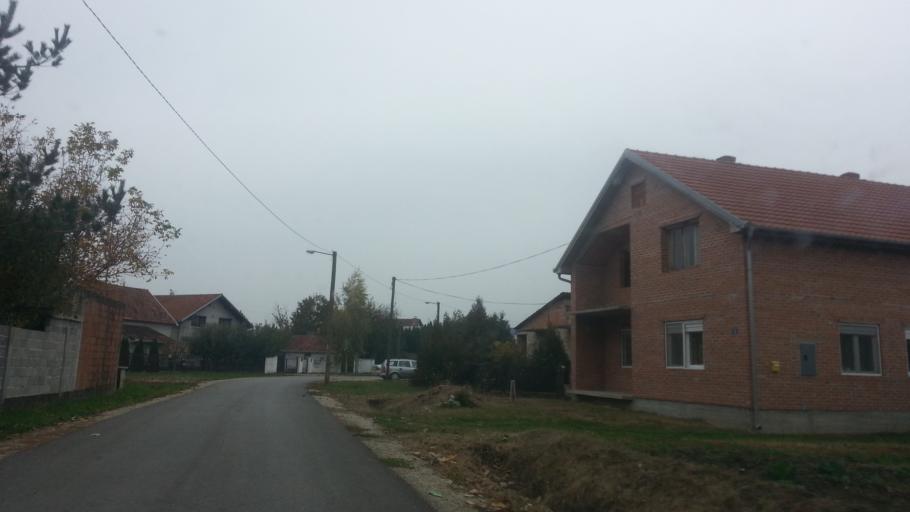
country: RS
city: Stari Banovci
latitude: 44.9815
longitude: 20.2721
